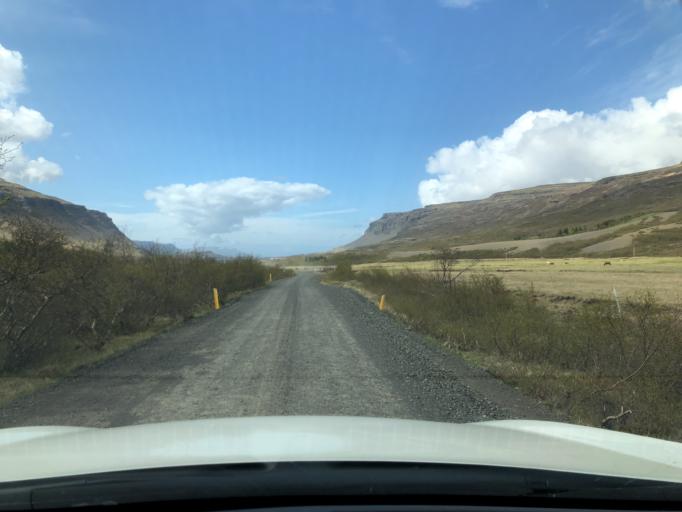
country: IS
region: South
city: Hveragerdi
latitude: 64.3860
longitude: -21.3120
